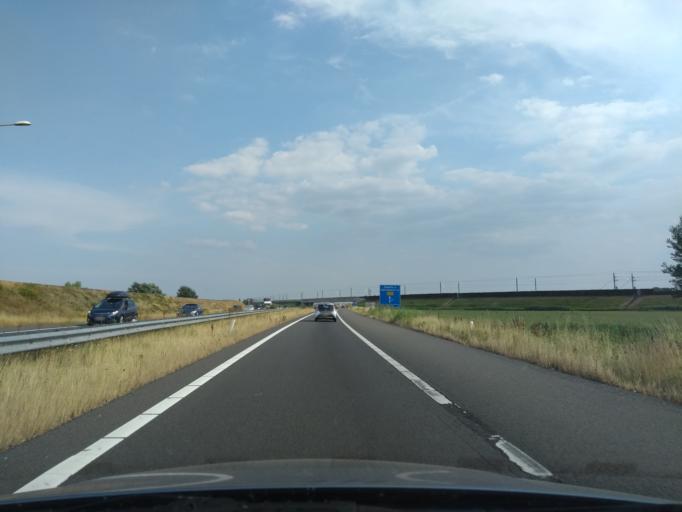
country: NL
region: Overijssel
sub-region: Gemeente Kampen
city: Kampen
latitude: 52.5379
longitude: 5.9044
